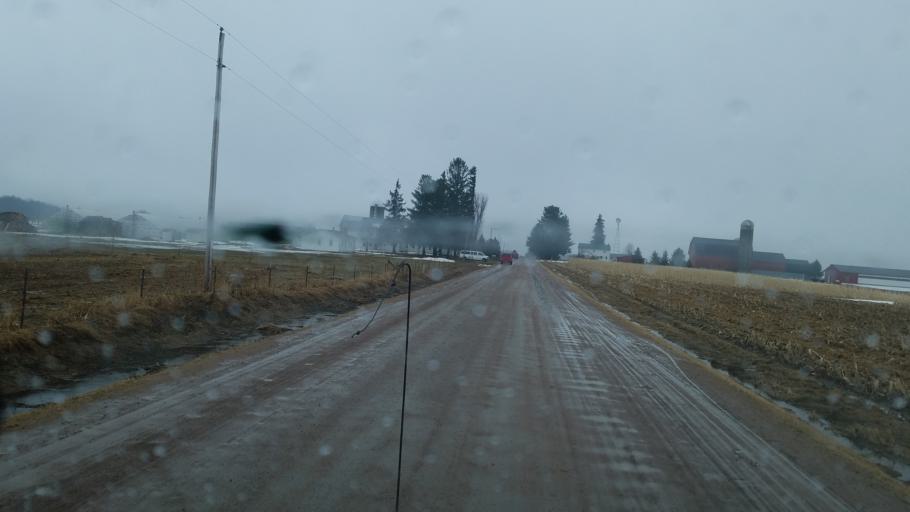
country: US
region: Wisconsin
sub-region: Clark County
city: Loyal
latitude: 44.6495
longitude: -90.3977
